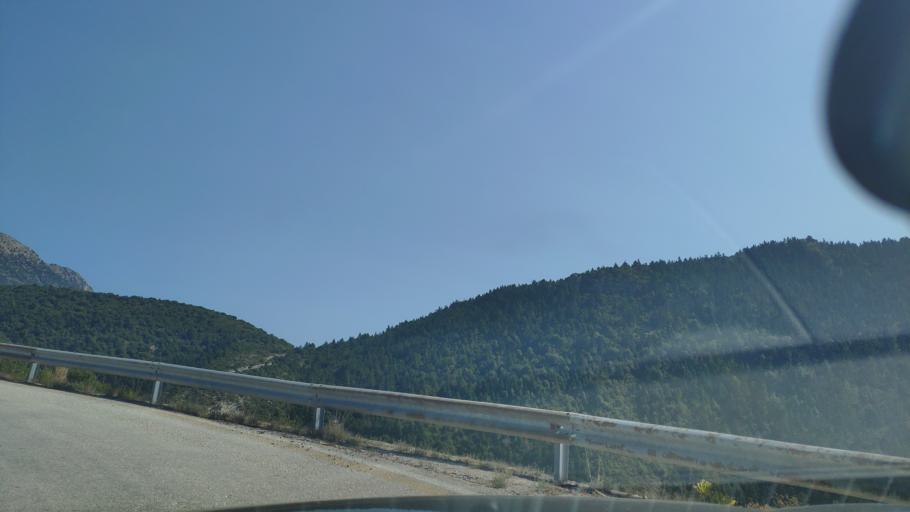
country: GR
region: Peloponnese
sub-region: Nomos Korinthias
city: Nemea
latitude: 37.8652
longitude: 22.3875
